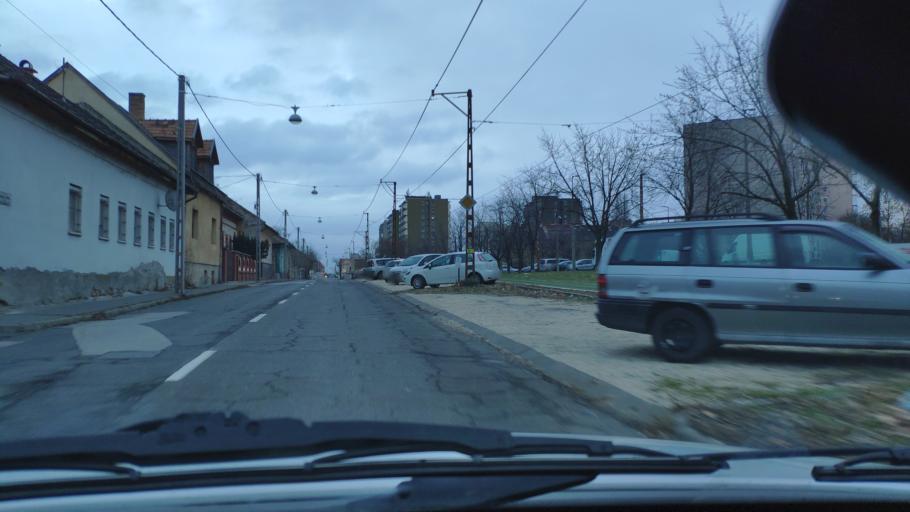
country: HU
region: Budapest
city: Budapest XX. keruelet
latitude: 47.4432
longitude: 19.1010
